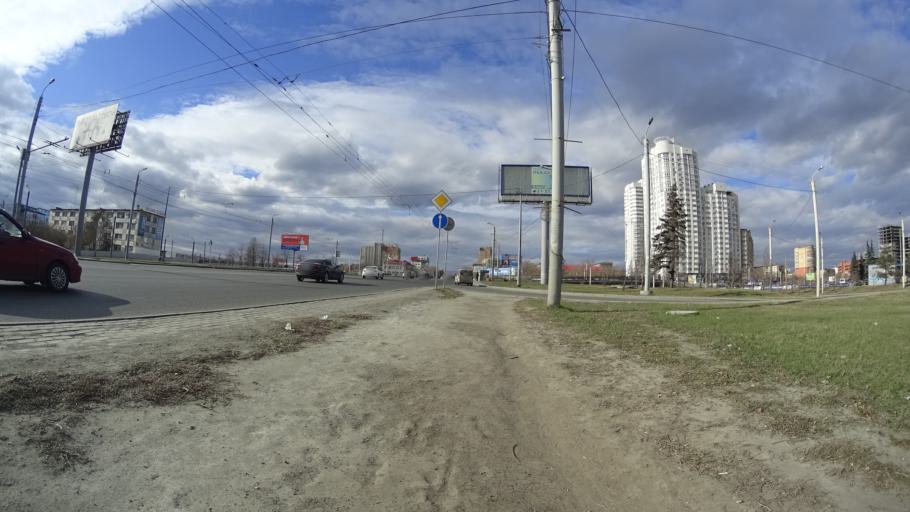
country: RU
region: Chelyabinsk
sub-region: Gorod Chelyabinsk
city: Chelyabinsk
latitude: 55.1727
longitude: 61.3880
